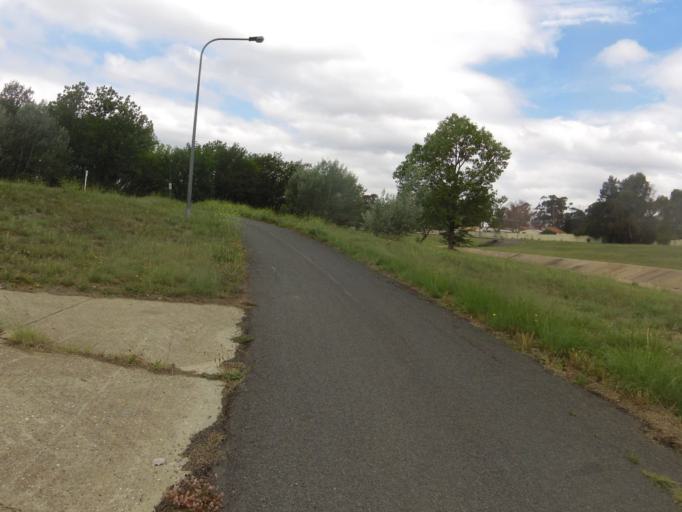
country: AU
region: Australian Capital Territory
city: Macarthur
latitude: -35.4221
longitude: 149.0948
